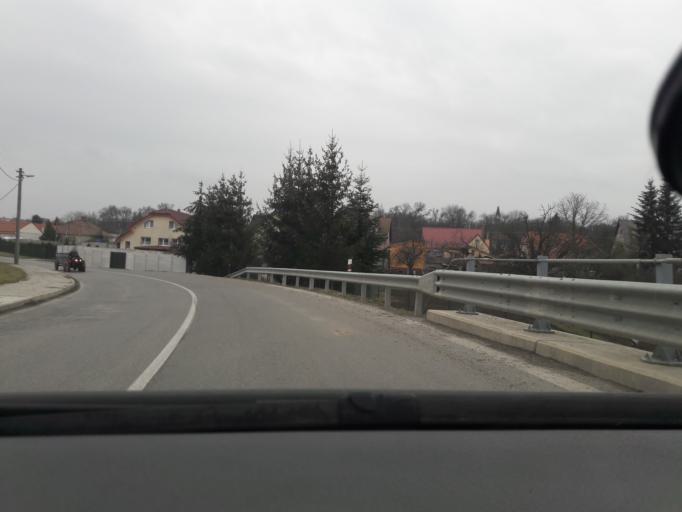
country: SK
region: Bratislavsky
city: Modra
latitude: 48.3665
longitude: 17.3995
